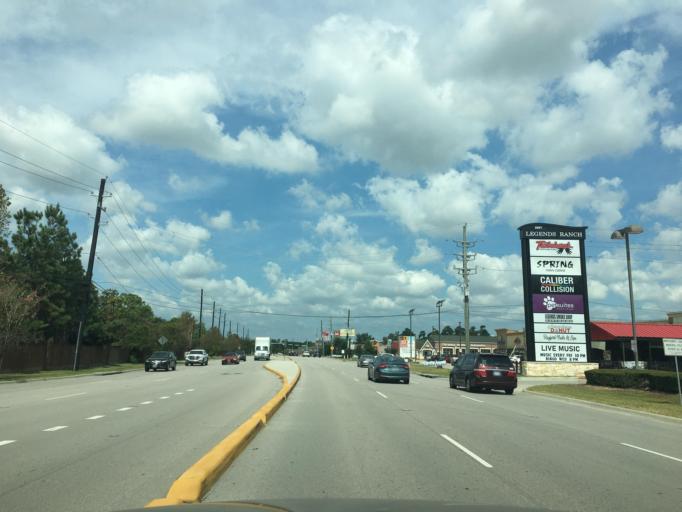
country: US
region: Texas
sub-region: Harris County
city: Spring
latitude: 30.1207
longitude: -95.3992
